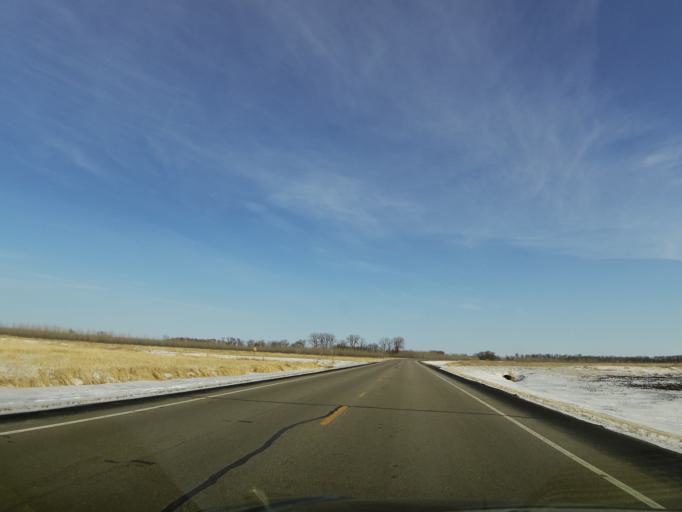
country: US
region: North Dakota
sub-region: Walsh County
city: Grafton
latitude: 48.4136
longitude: -97.1194
